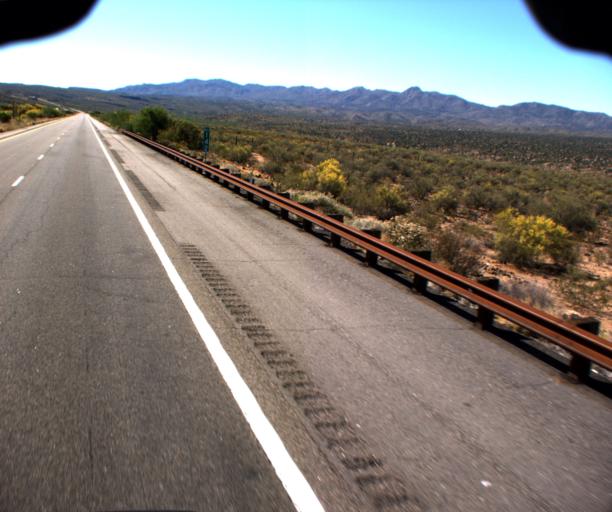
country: US
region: Arizona
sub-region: Yavapai County
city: Bagdad
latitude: 34.5249
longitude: -113.4265
